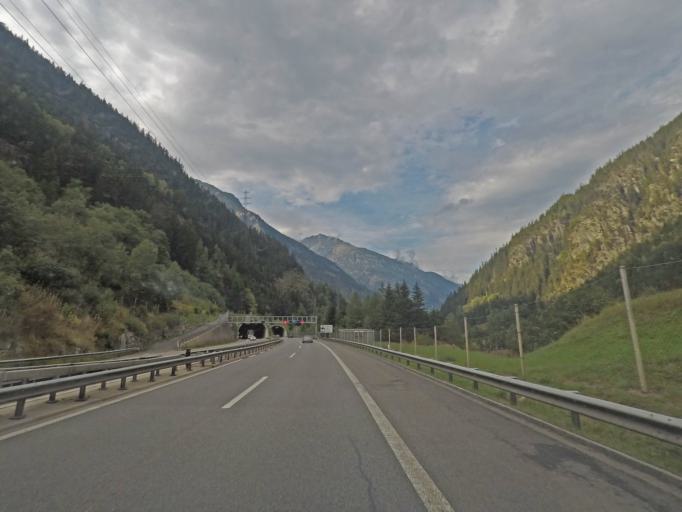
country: CH
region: Uri
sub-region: Uri
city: Andermatt
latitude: 46.6811
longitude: 8.5926
